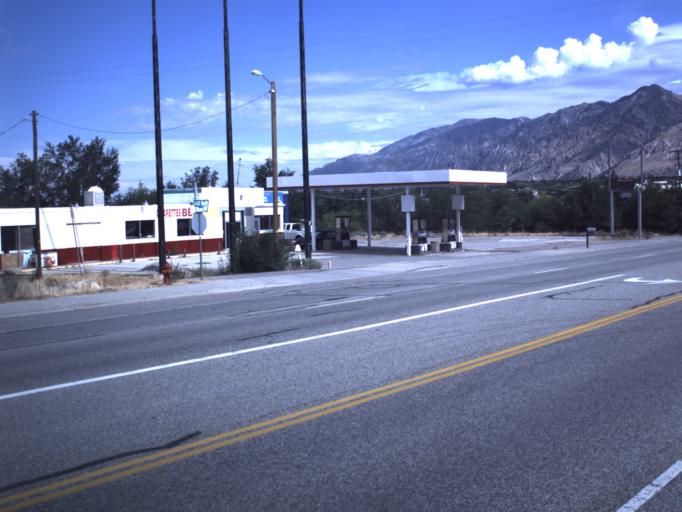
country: US
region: Utah
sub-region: Box Elder County
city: Perry
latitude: 41.4840
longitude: -112.0175
